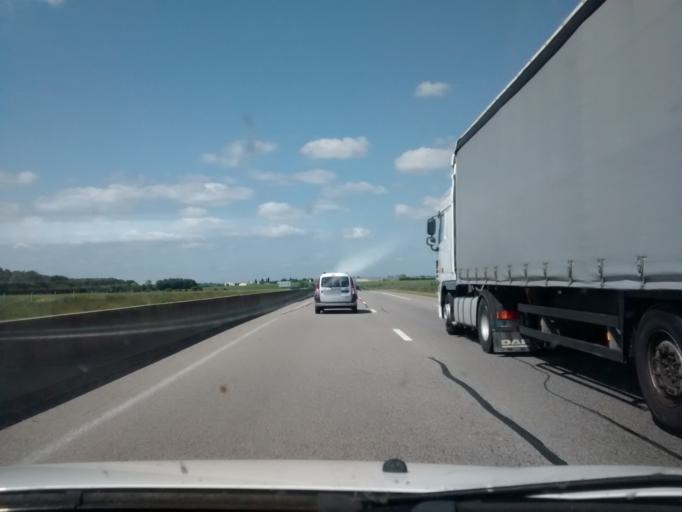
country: FR
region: Ile-de-France
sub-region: Departement des Yvelines
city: Ablis
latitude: 48.5523
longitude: 1.8303
